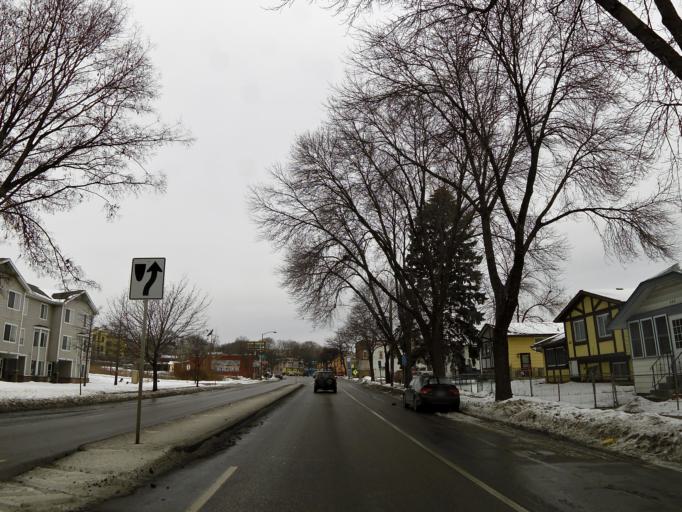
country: US
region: Minnesota
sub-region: Ramsey County
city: Saint Paul
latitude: 44.9292
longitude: -93.0755
